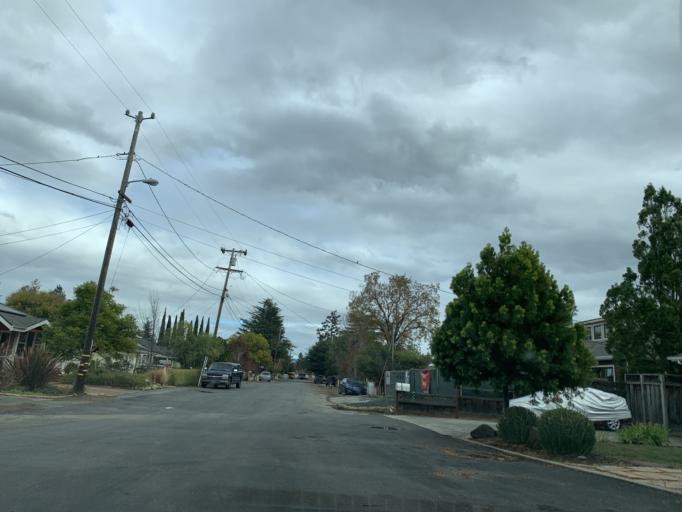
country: US
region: California
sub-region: Santa Clara County
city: Campbell
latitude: 37.2708
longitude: -121.9745
